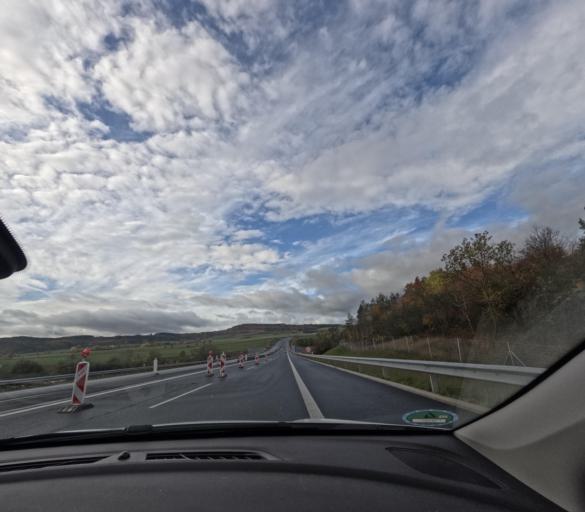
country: CZ
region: Ustecky
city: Lubenec
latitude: 50.1361
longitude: 13.3054
